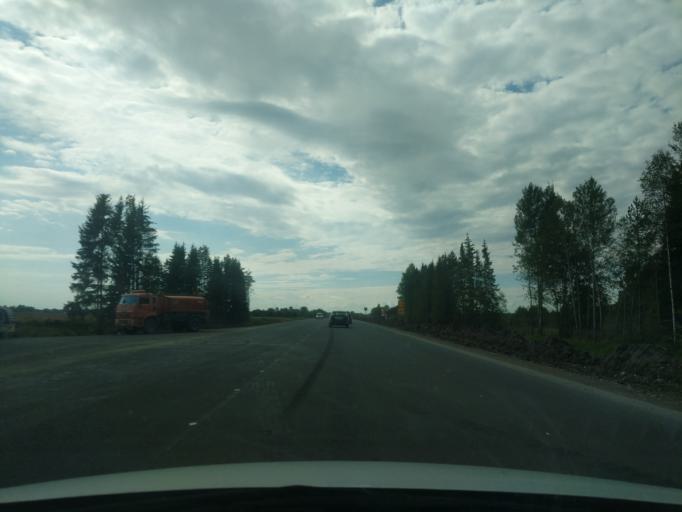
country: RU
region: Kostroma
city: Sudislavl'
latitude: 57.8386
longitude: 41.5633
